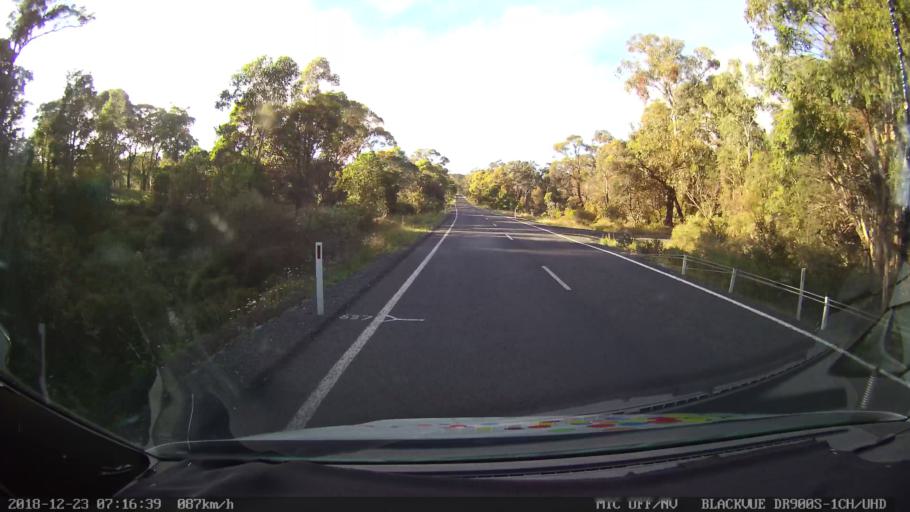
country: AU
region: New South Wales
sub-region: Bellingen
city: Dorrigo
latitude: -30.4585
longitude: 152.3083
